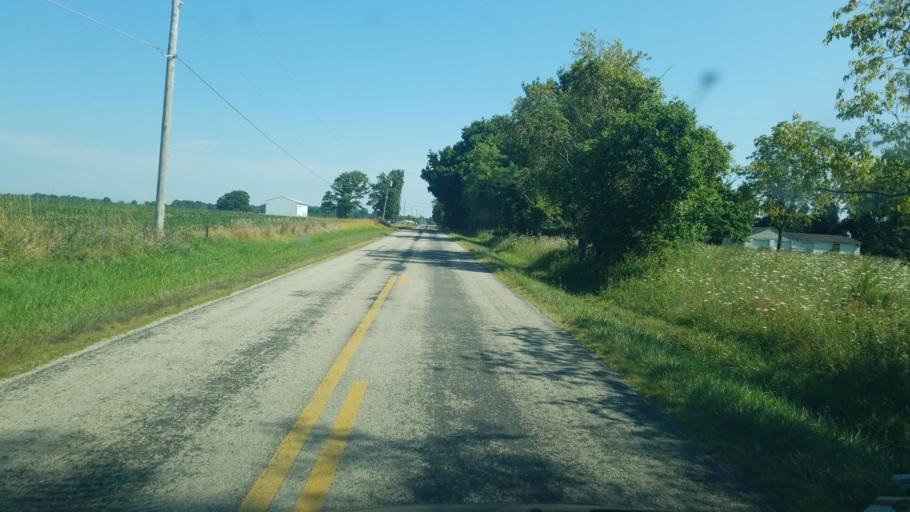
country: US
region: Ohio
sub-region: Delaware County
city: Lewis Center
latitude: 40.2650
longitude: -82.9644
